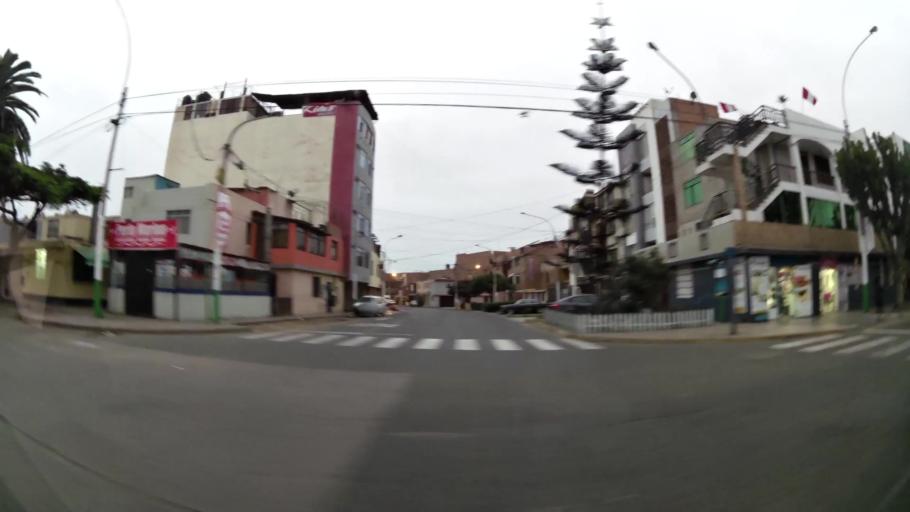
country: PE
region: Callao
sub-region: Callao
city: Callao
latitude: -12.0669
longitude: -77.1088
